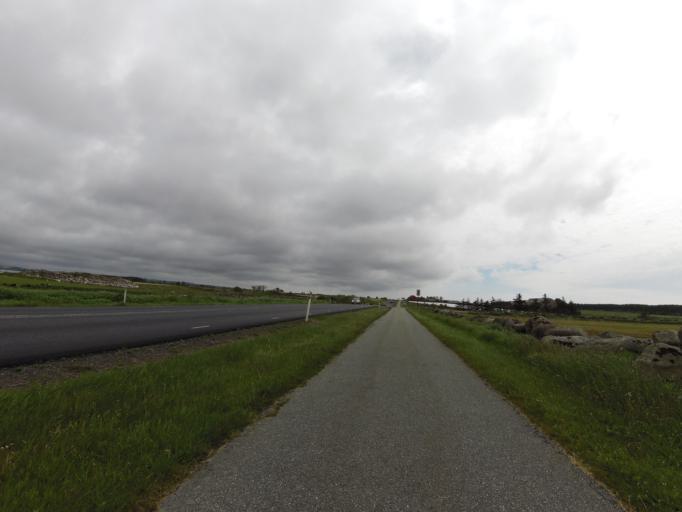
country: NO
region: Rogaland
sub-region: Ha
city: Naerbo
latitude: 58.6427
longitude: 5.6048
